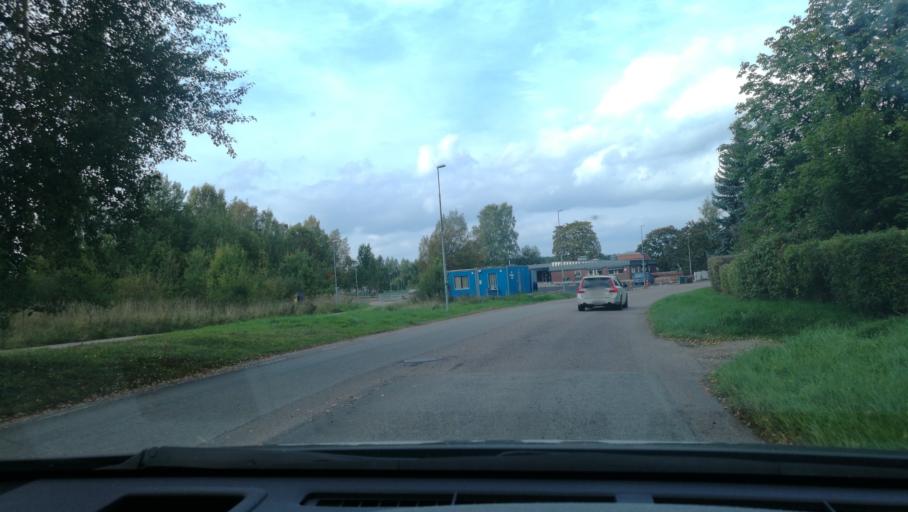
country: SE
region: Dalarna
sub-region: Avesta Kommun
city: Avesta
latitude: 60.1608
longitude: 16.1932
